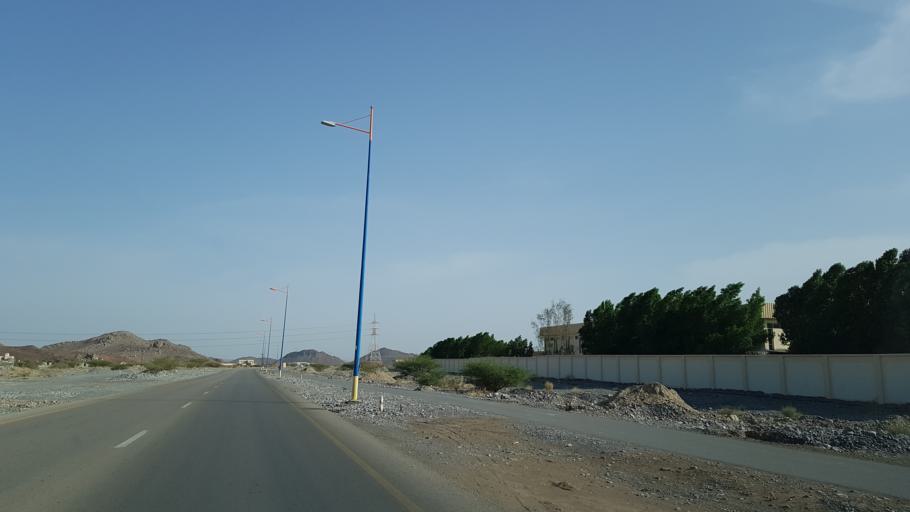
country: OM
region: Muhafazat ad Dakhiliyah
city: Izki
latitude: 22.9115
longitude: 57.6748
